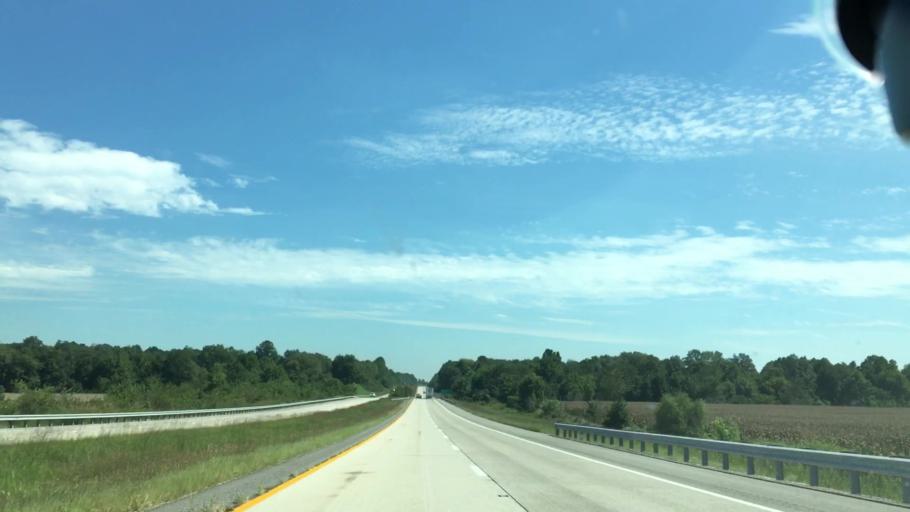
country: US
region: Kentucky
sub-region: Henderson County
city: Henderson
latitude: 37.7820
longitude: -87.4595
